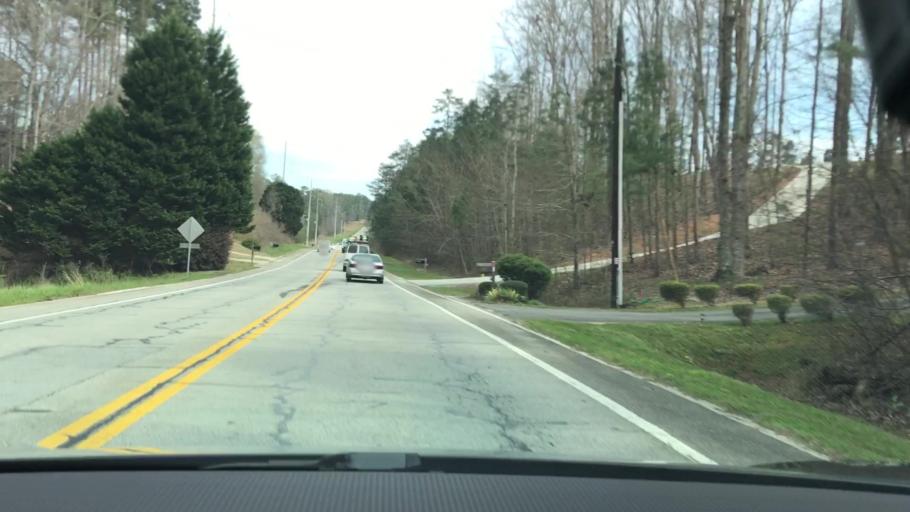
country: US
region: Georgia
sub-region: Gwinnett County
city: Sugar Hill
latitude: 34.1493
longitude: -84.0372
